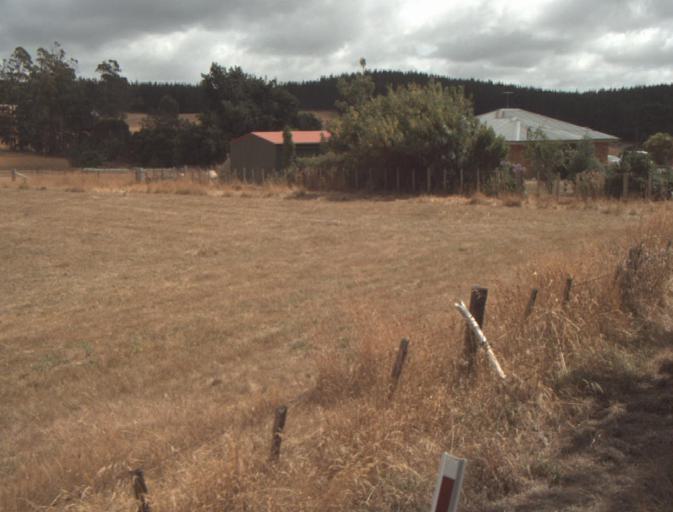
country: AU
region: Tasmania
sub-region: Launceston
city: Mayfield
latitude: -41.1733
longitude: 147.2124
